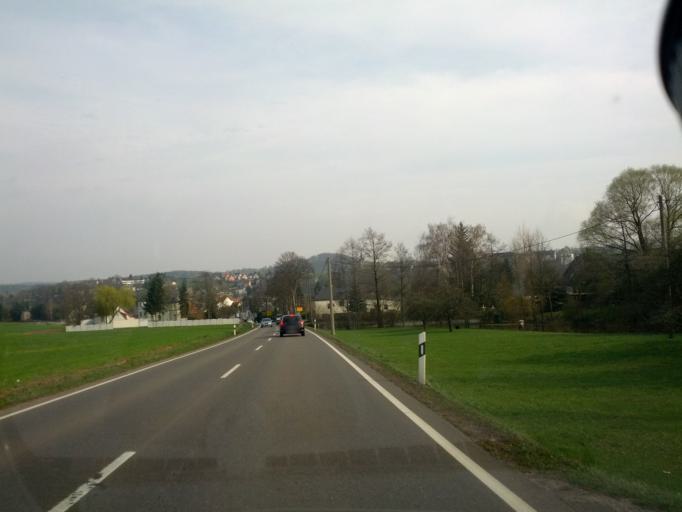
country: DE
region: Saxony
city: Wildenfels
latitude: 50.6715
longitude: 12.5985
